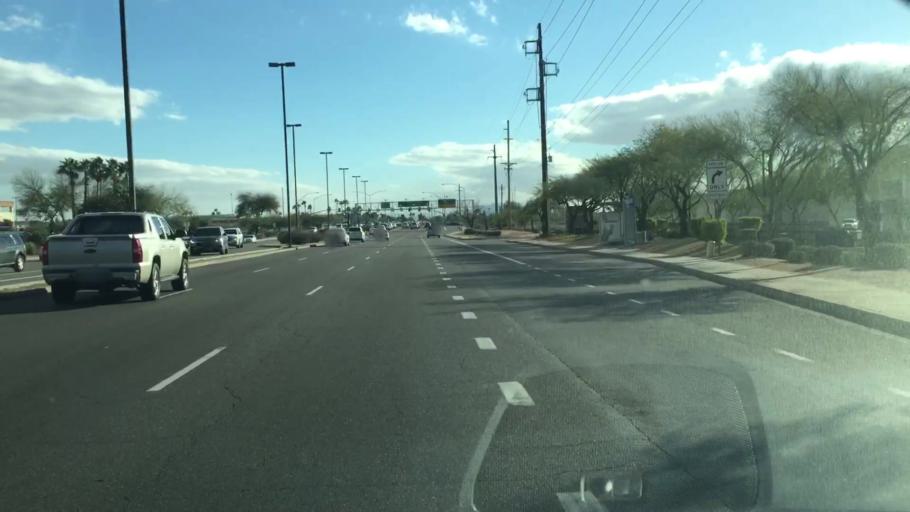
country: US
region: Arizona
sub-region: Maricopa County
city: Gilbert
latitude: 33.3900
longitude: -111.6849
